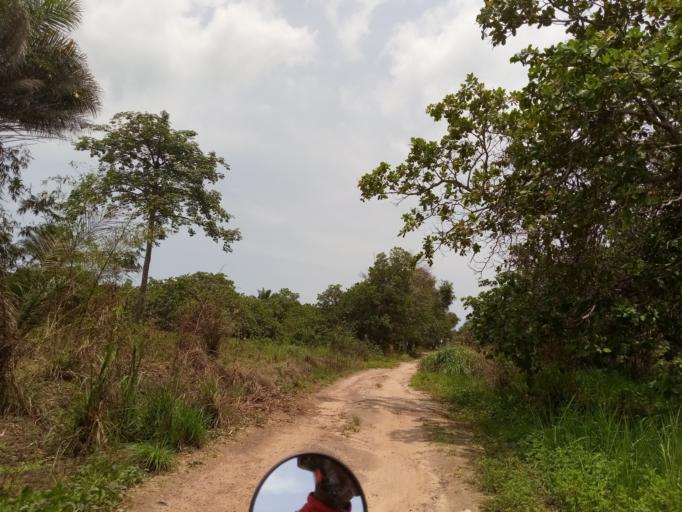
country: SL
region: Western Area
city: Waterloo
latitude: 8.3189
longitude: -13.0347
